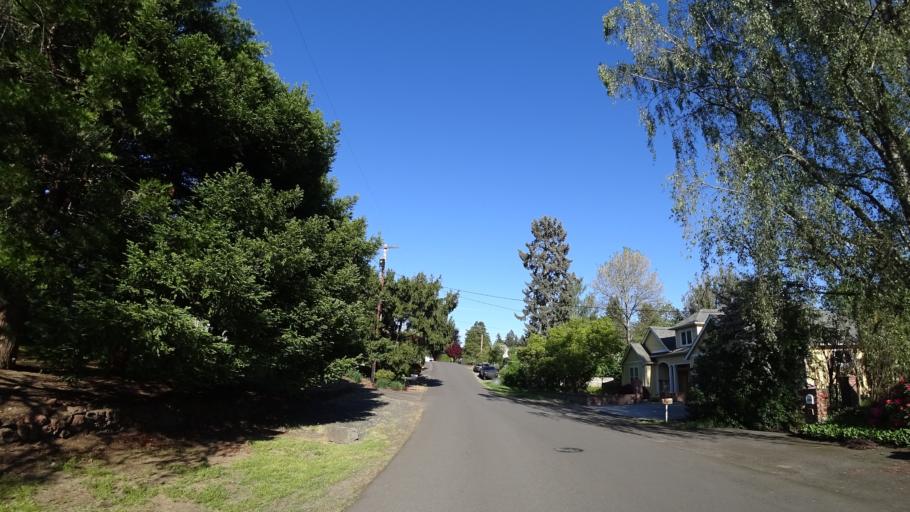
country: US
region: Oregon
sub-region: Washington County
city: West Slope
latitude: 45.4962
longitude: -122.7628
